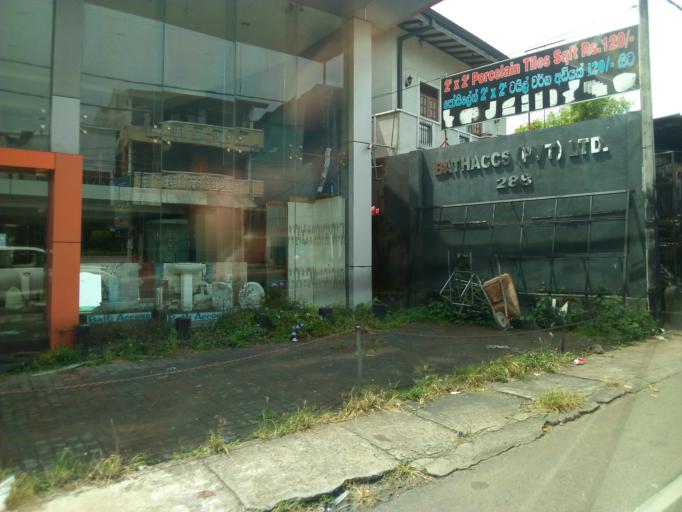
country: LK
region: Western
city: Galkissa
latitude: 6.8431
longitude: 79.8847
